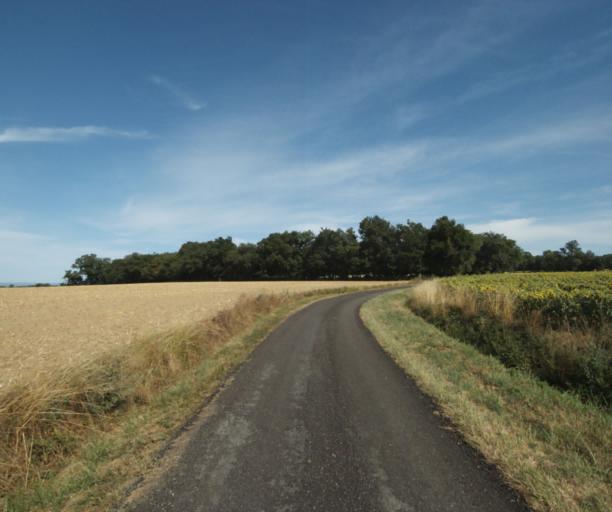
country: FR
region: Midi-Pyrenees
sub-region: Departement du Tarn
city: Soreze
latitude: 43.5124
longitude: 2.0522
